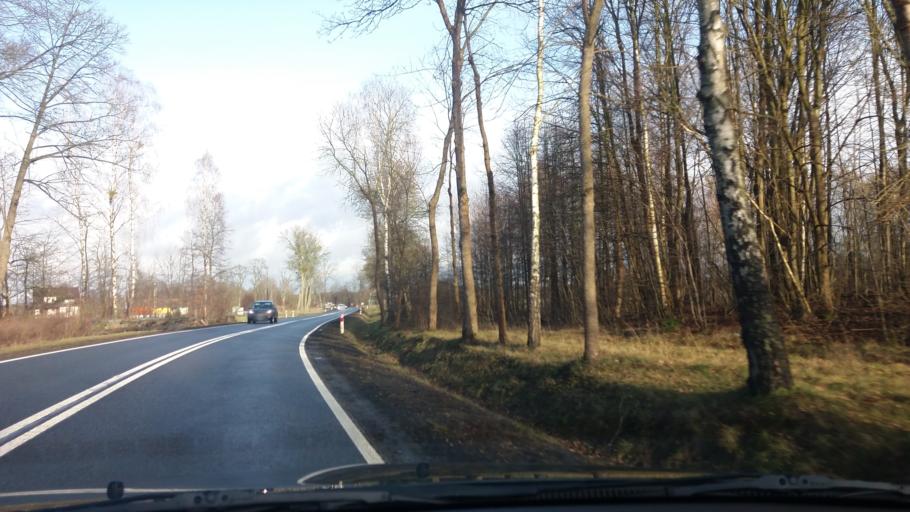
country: PL
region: Masovian Voivodeship
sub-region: Powiat przasnyski
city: Chorzele
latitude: 53.2855
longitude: 20.9048
